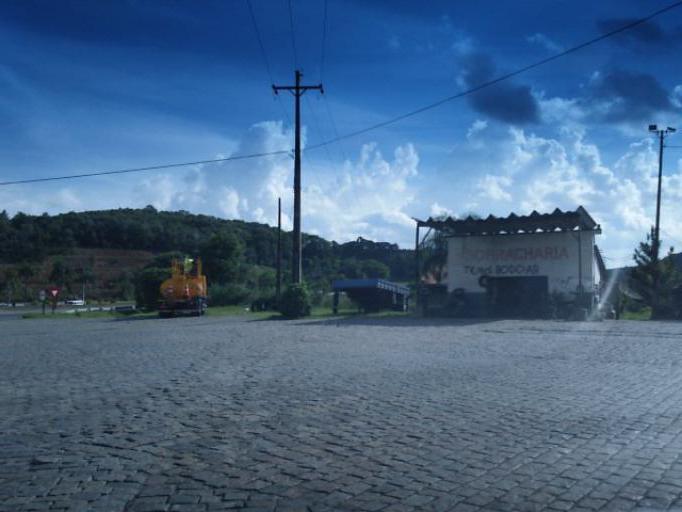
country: BR
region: Parana
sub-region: Campina Grande Do Sul
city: Campina Grande do Sul
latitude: -25.3161
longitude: -49.0186
